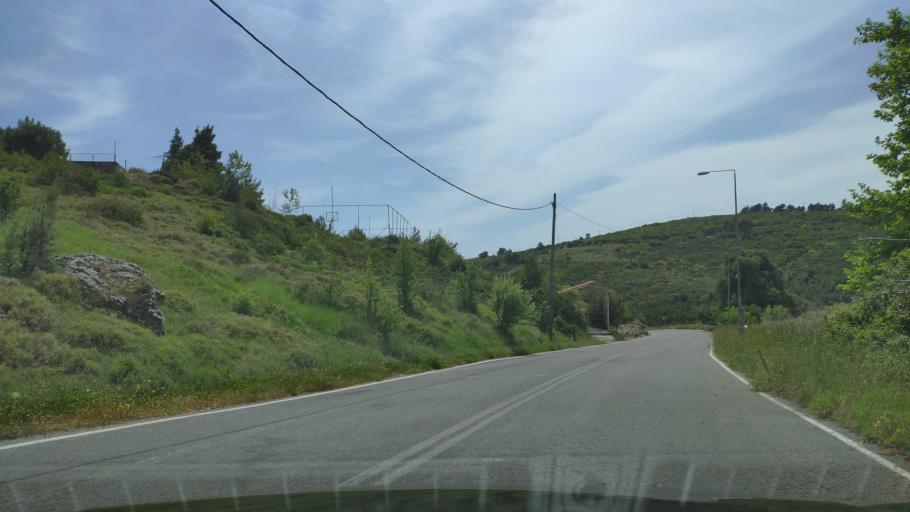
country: GR
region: Attica
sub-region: Nomarchia Anatolikis Attikis
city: Varnavas
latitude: 38.2221
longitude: 23.9274
